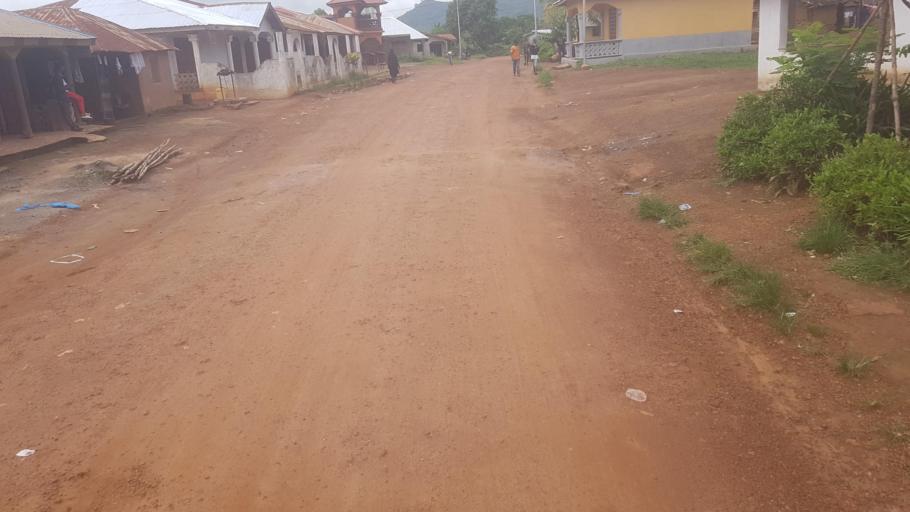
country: SL
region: Southern Province
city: Mogbwemo
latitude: 7.7612
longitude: -12.3061
